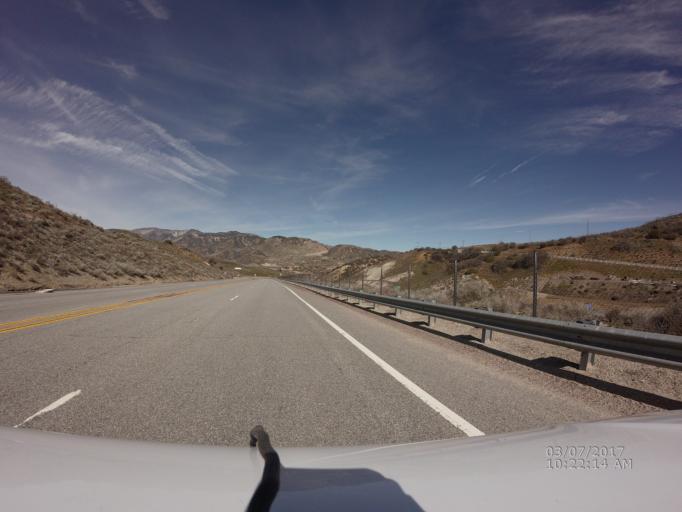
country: US
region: California
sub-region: Kern County
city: Lebec
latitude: 34.8037
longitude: -118.8787
